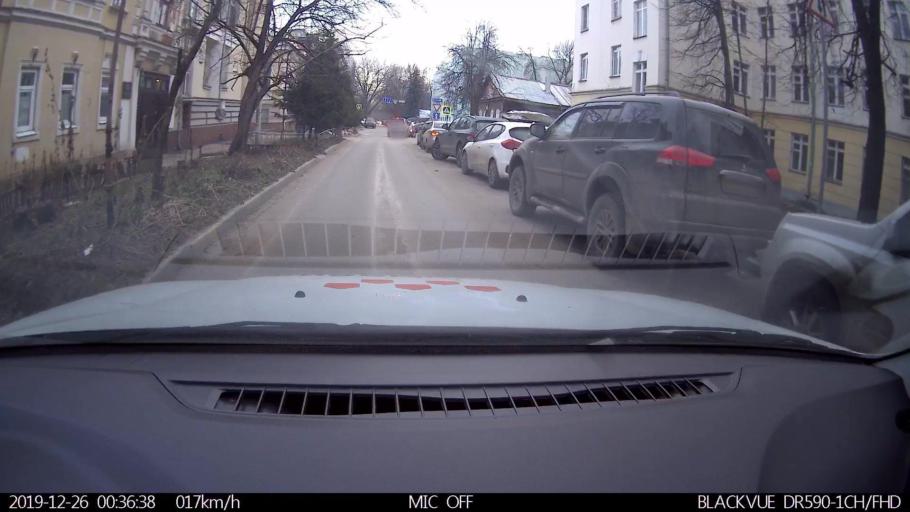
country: RU
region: Nizjnij Novgorod
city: Nizhniy Novgorod
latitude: 56.3241
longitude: 44.0189
